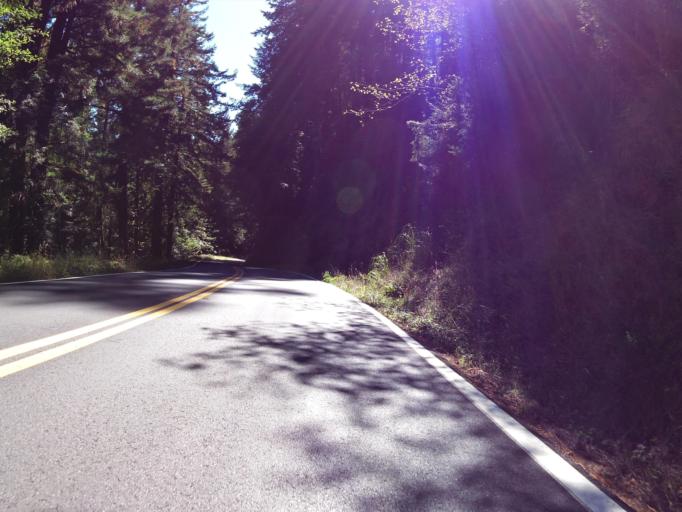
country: US
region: California
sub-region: Mendocino County
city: Fort Bragg
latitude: 39.7188
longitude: -123.8015
